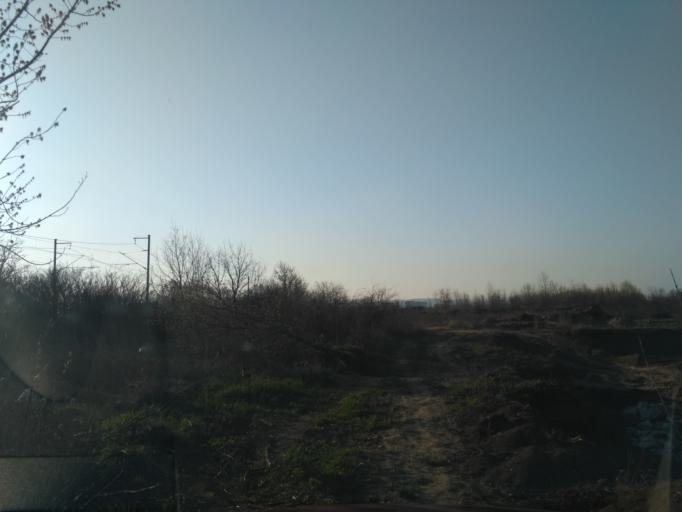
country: SK
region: Kosicky
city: Kosice
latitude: 48.6628
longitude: 21.3097
